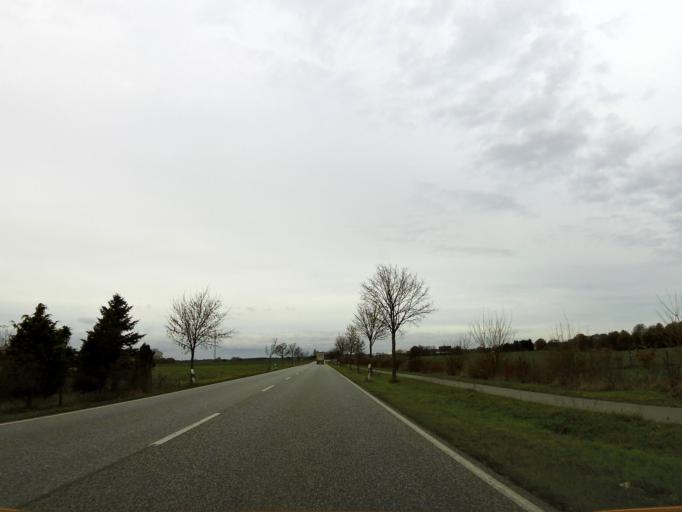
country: DE
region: Saxony-Anhalt
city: Pretzier
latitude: 52.8065
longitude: 11.2241
